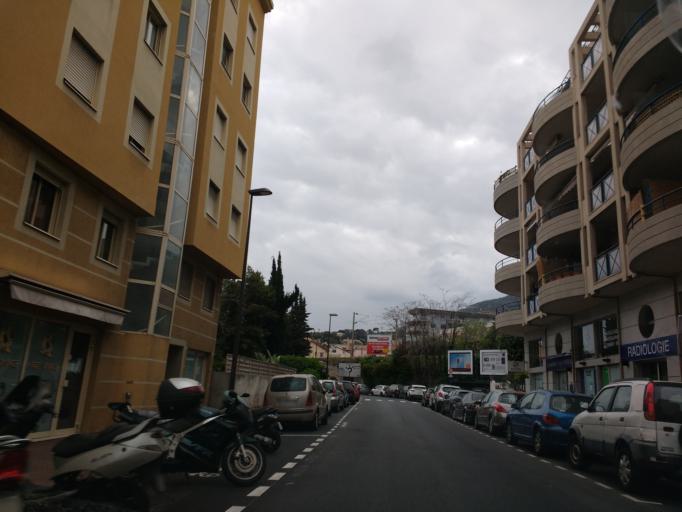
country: FR
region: Provence-Alpes-Cote d'Azur
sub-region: Departement des Alpes-Maritimes
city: Roquebrune-Cap-Martin
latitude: 43.7658
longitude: 7.4862
